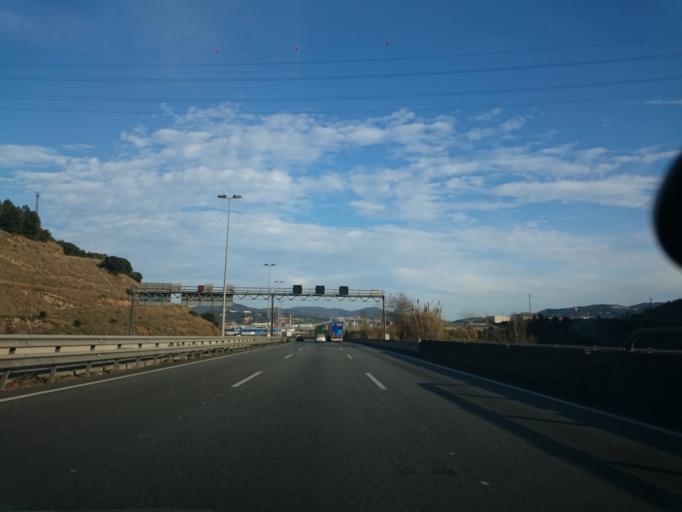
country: ES
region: Catalonia
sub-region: Provincia de Barcelona
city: Martorell
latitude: 41.4717
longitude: 1.9420
